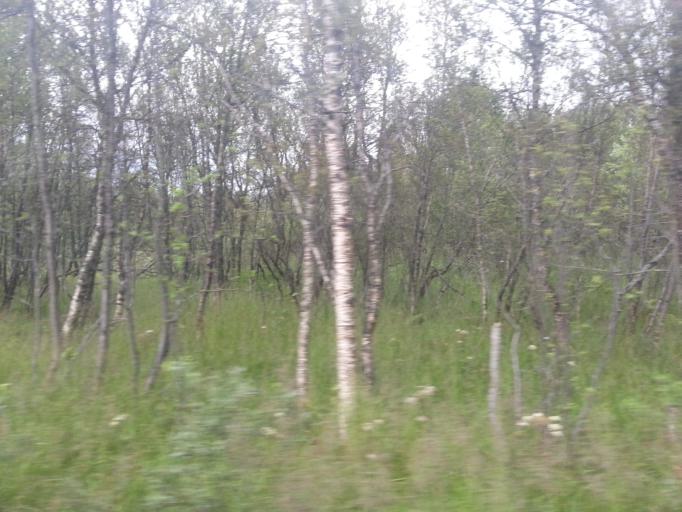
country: NO
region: Troms
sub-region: Tromso
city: Tromso
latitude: 69.6553
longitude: 18.9348
